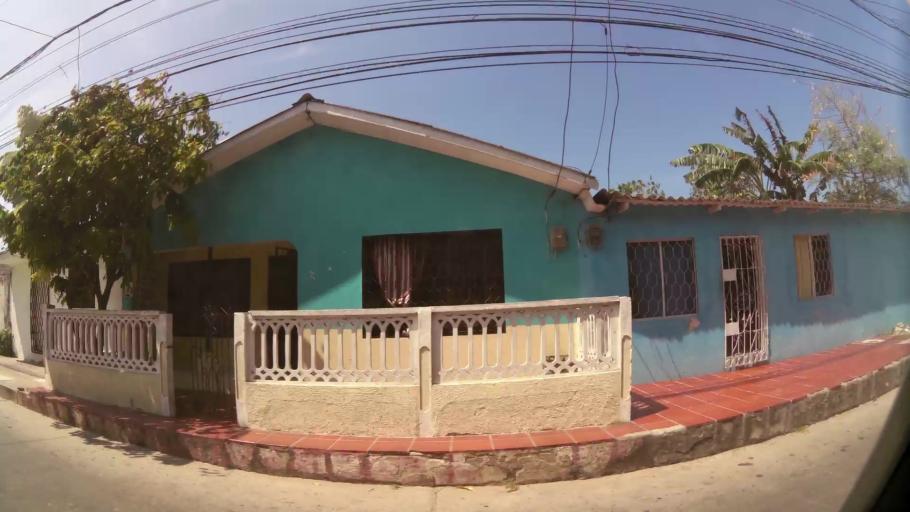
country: CO
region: Atlantico
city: Barranquilla
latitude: 10.9629
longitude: -74.8076
